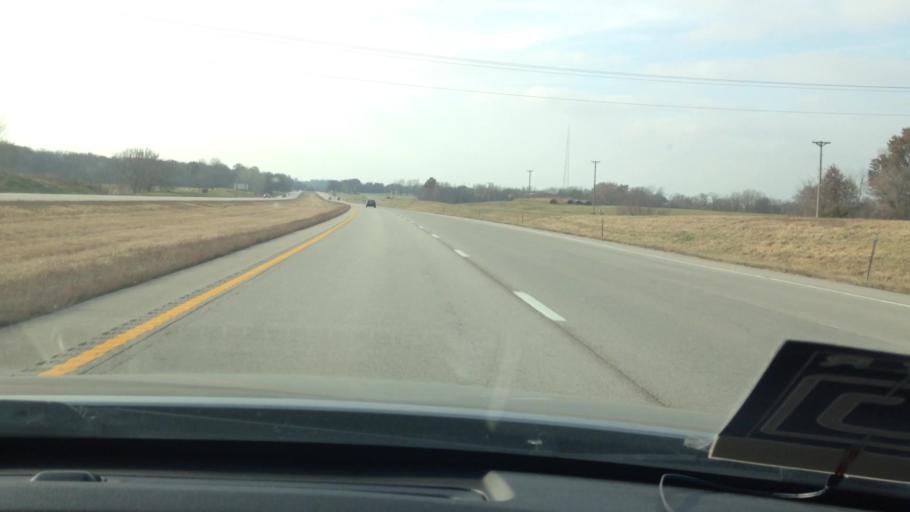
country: US
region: Missouri
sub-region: Cass County
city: Garden City
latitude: 38.5023
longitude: -94.0752
